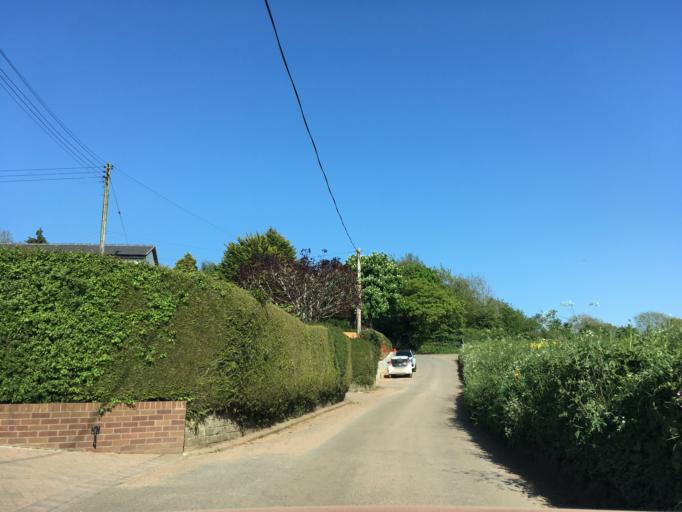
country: GB
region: Wales
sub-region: Monmouthshire
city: Chepstow
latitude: 51.6373
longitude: -2.6956
